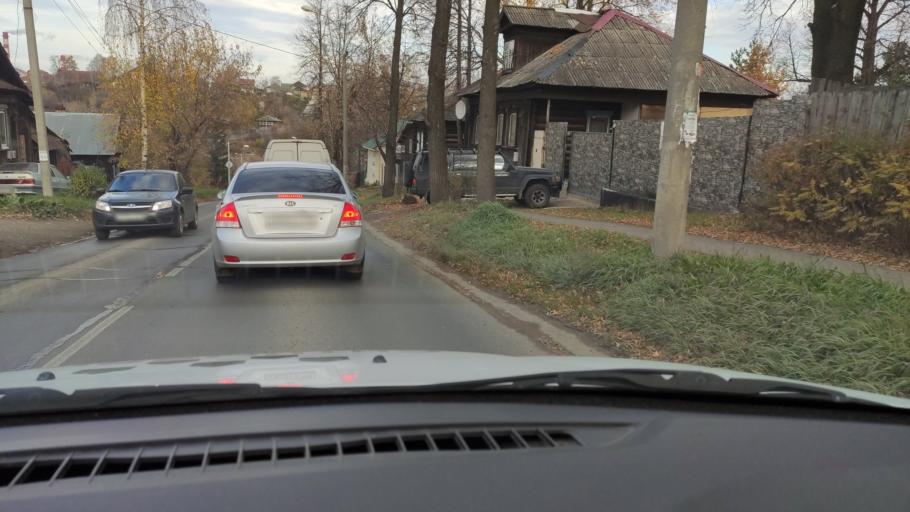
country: RU
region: Perm
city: Perm
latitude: 58.0387
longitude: 56.3290
